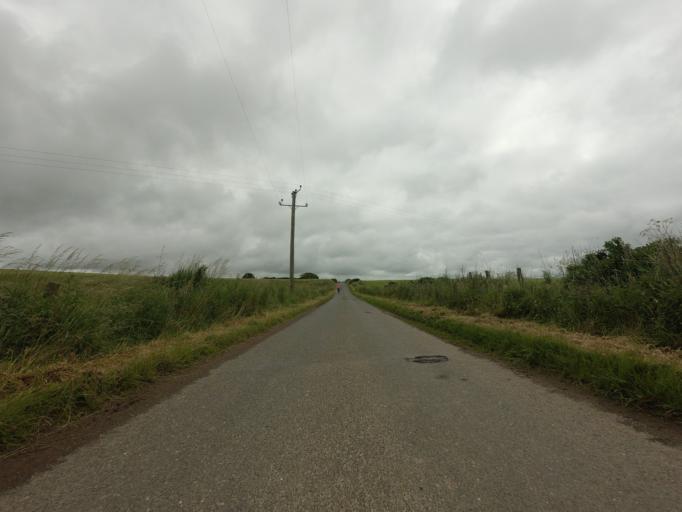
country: GB
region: Scotland
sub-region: Aberdeenshire
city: Turriff
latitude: 57.5445
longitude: -2.2792
